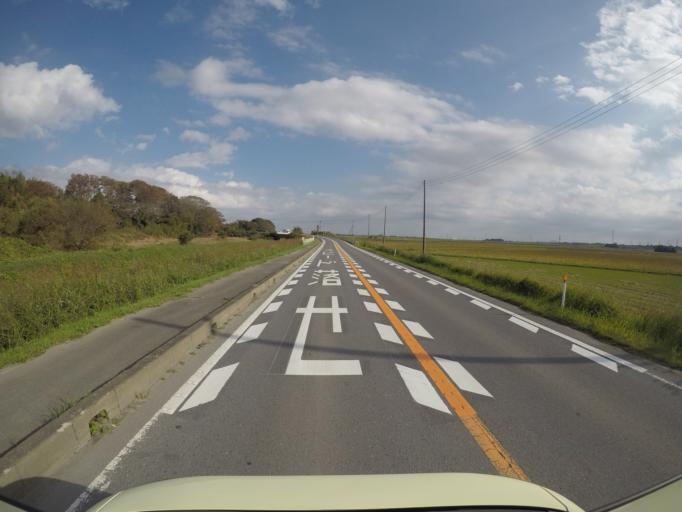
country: JP
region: Ibaraki
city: Iwai
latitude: 35.9895
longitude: 139.9088
